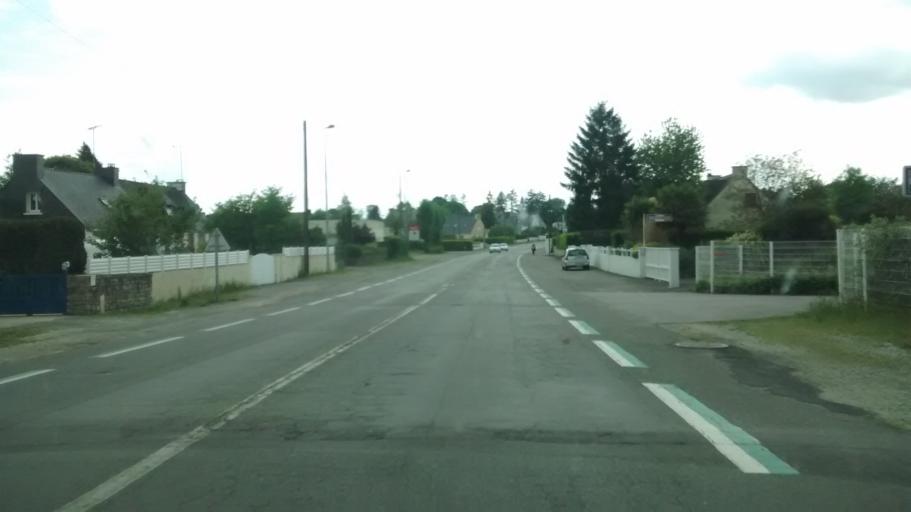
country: FR
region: Brittany
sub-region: Departement du Morbihan
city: Questembert
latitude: 47.6677
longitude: -2.4500
